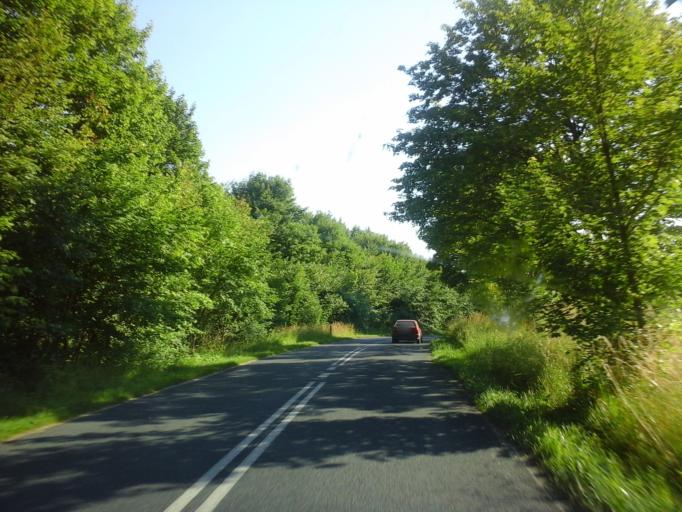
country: PL
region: West Pomeranian Voivodeship
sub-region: Powiat stargardzki
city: Dobrzany
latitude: 53.4184
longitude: 15.4250
